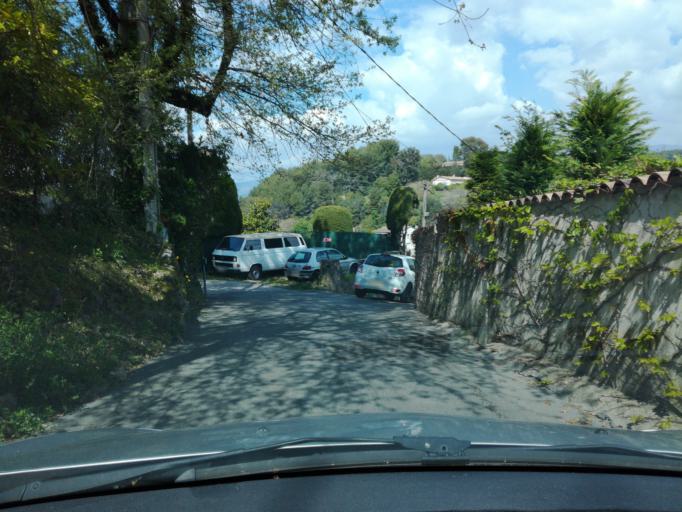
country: FR
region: Provence-Alpes-Cote d'Azur
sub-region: Departement des Alpes-Maritimes
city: Mougins
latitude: 43.6045
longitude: 6.9950
